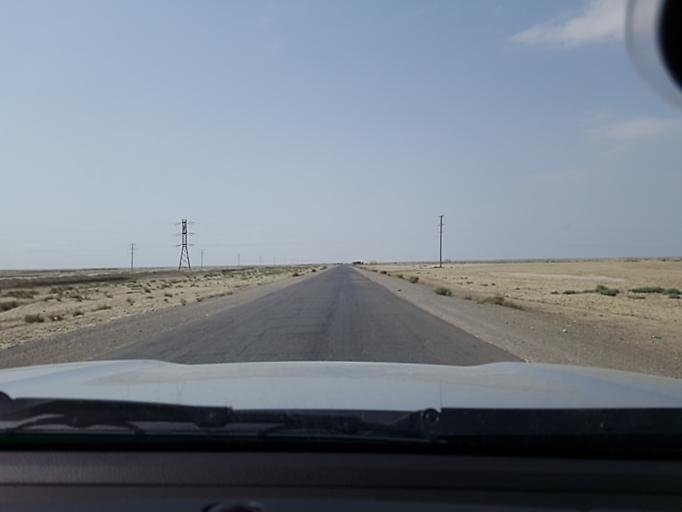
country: TM
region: Balkan
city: Gumdag
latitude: 39.0020
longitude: 54.5861
